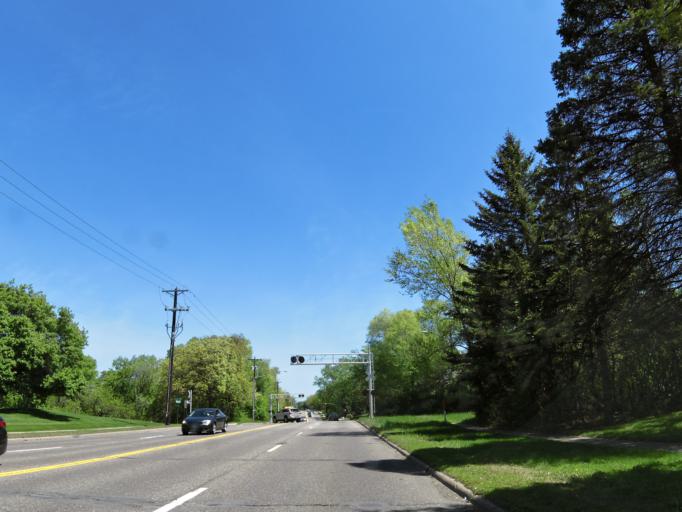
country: US
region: Minnesota
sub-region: Scott County
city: Savage
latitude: 44.8079
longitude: -93.3474
